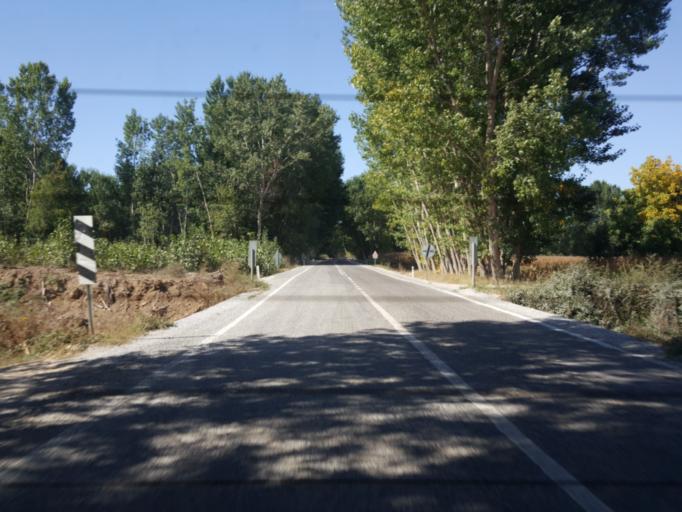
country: TR
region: Tokat
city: Pazar
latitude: 40.2685
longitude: 36.2132
